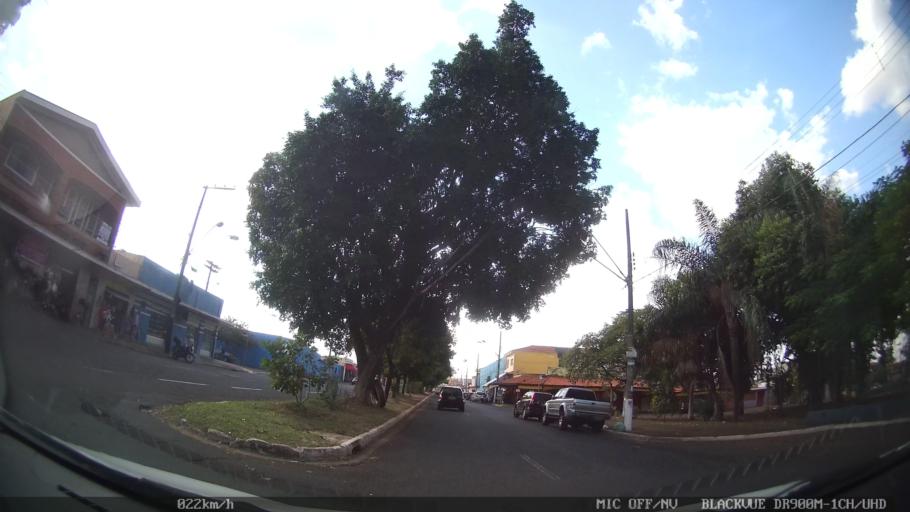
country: BR
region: Sao Paulo
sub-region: Ribeirao Preto
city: Ribeirao Preto
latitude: -21.1937
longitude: -47.8386
